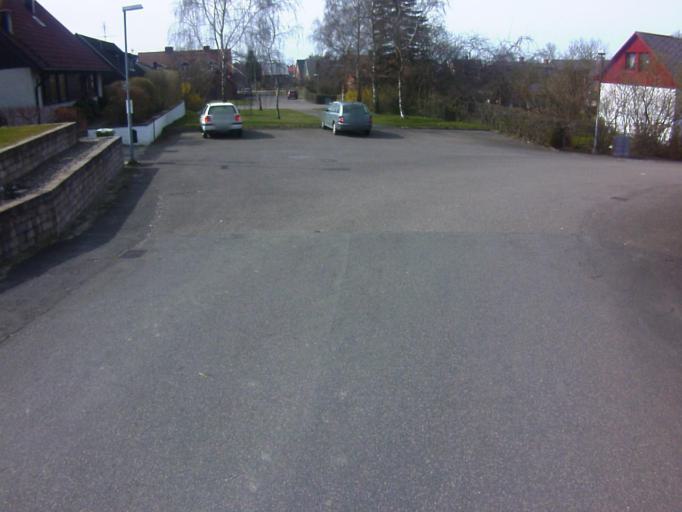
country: SE
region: Skane
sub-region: Kavlinge Kommun
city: Kaevlinge
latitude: 55.7788
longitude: 13.1099
